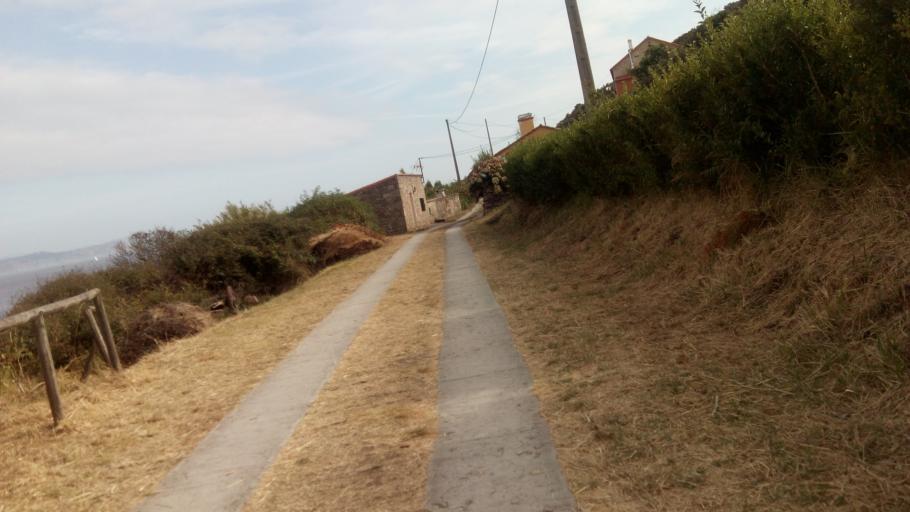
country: ES
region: Galicia
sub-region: Provincia de Pontevedra
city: Sanxenxo
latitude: 42.3684
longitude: -8.9349
